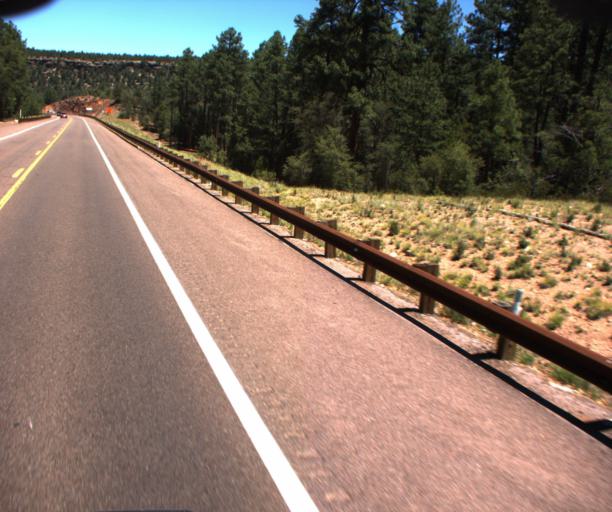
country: US
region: Arizona
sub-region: Gila County
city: Payson
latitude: 34.2730
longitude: -111.3218
